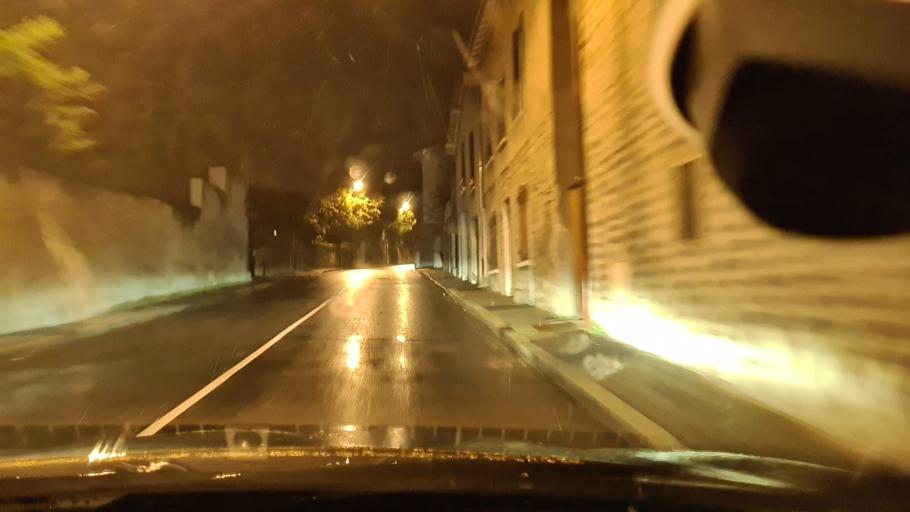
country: FR
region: Rhone-Alpes
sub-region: Departement du Rhone
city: Limonest
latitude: 45.8124
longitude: 4.7979
